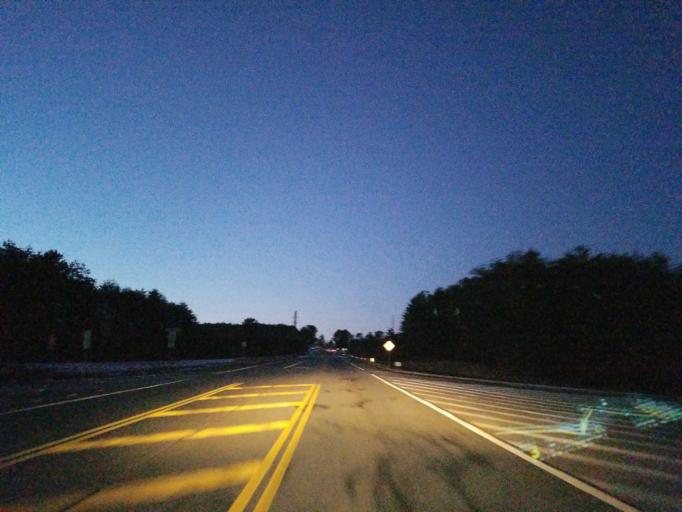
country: US
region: Georgia
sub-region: Cherokee County
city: Ball Ground
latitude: 34.3004
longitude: -84.4234
